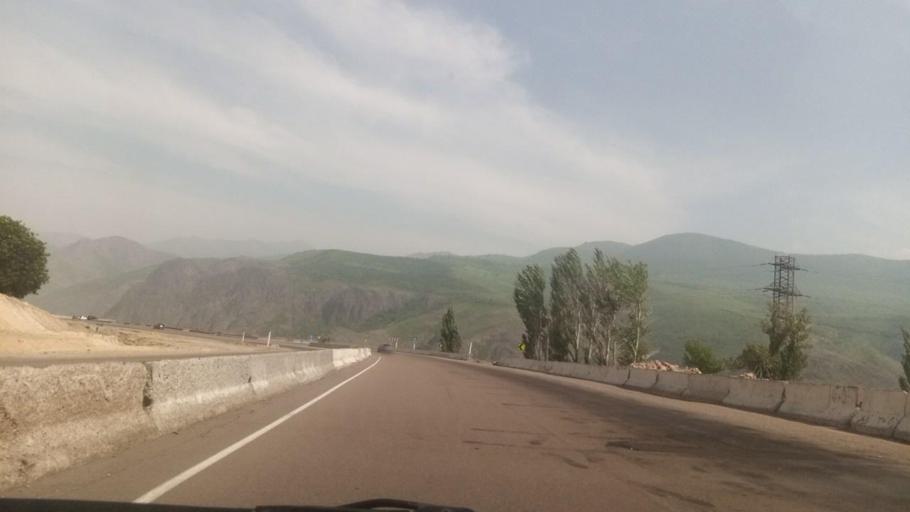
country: UZ
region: Toshkent
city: Angren
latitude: 41.0696
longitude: 70.2378
